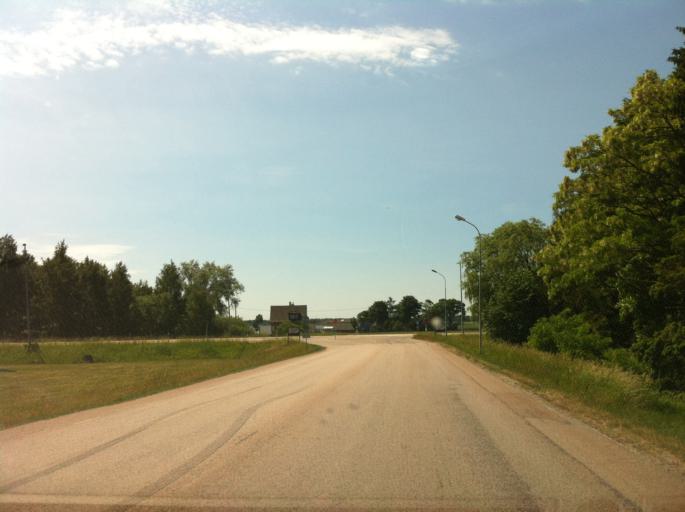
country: SE
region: Skane
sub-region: Bjuvs Kommun
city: Bjuv
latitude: 56.0767
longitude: 12.9098
